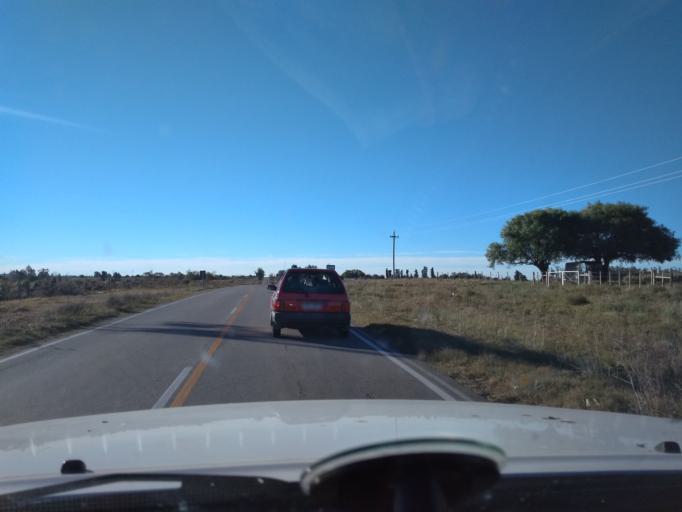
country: UY
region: Canelones
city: San Ramon
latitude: -34.3512
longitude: -55.9594
